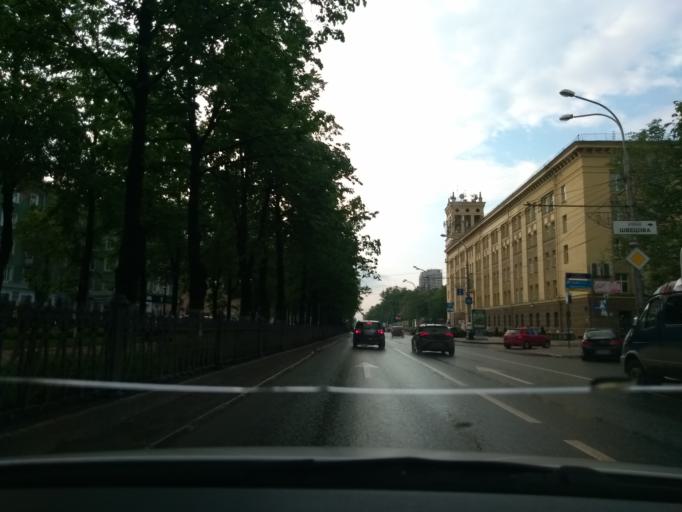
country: RU
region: Perm
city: Perm
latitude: 58.0014
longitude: 56.2485
